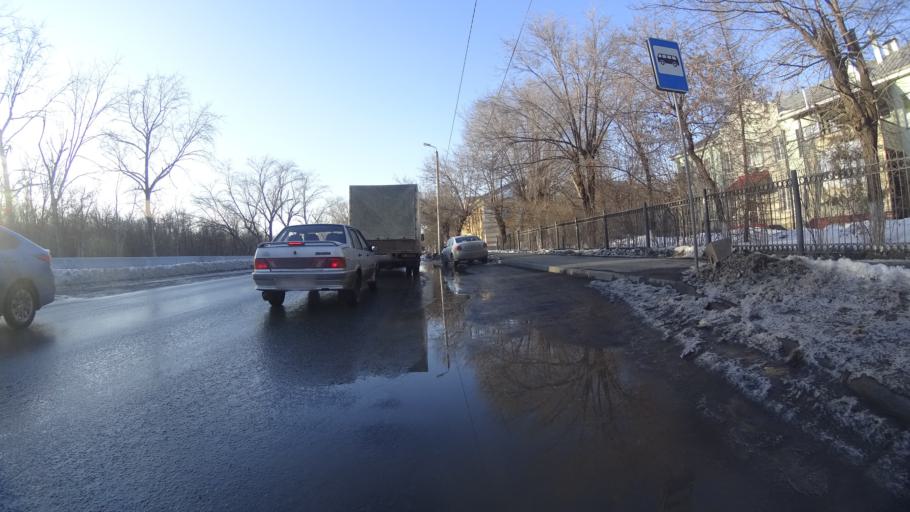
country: RU
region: Chelyabinsk
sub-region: Gorod Chelyabinsk
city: Chelyabinsk
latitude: 55.1339
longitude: 61.4595
